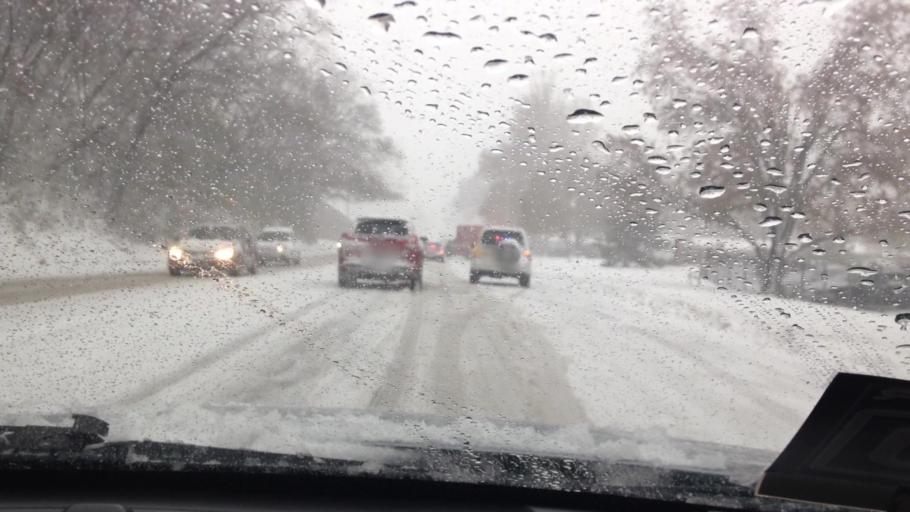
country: US
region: Kansas
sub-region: Johnson County
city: Westwood
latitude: 39.0626
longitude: -94.6131
